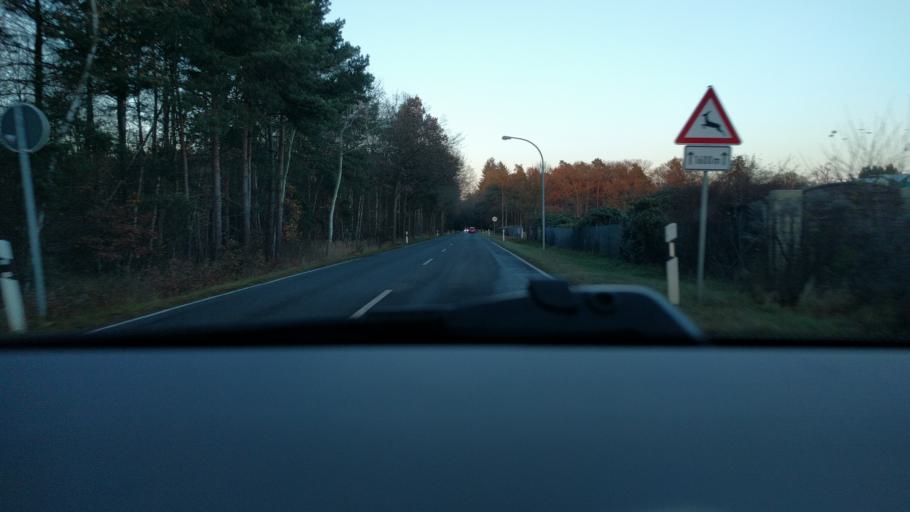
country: DE
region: Lower Saxony
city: Bokensdorf
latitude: 52.5551
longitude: 10.7187
